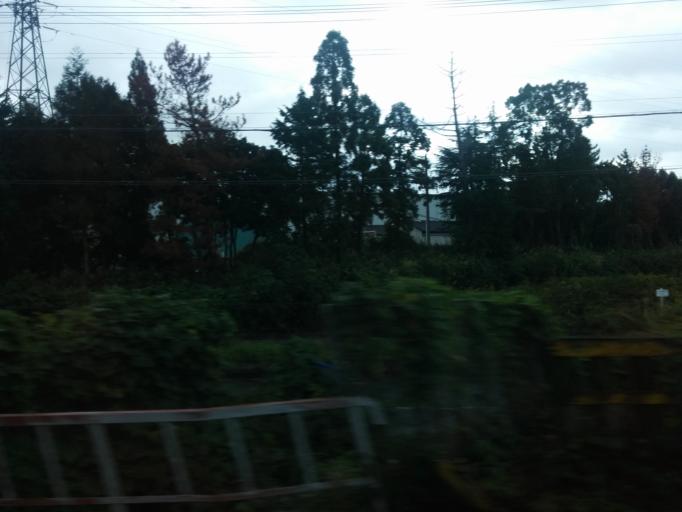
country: JP
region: Shiga Prefecture
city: Omihachiman
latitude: 35.0853
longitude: 136.0476
